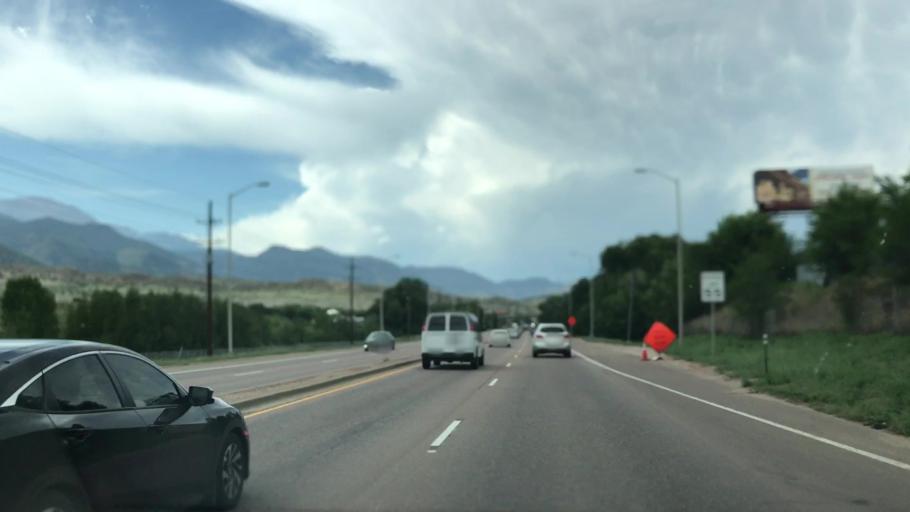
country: US
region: Colorado
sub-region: El Paso County
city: Colorado Springs
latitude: 38.8367
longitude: -104.8516
